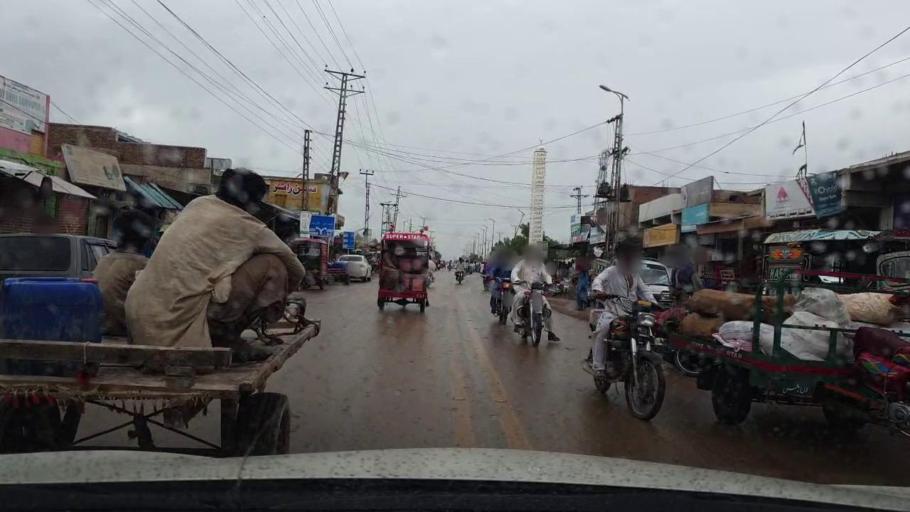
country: PK
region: Sindh
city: Kario
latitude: 24.6534
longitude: 68.5352
